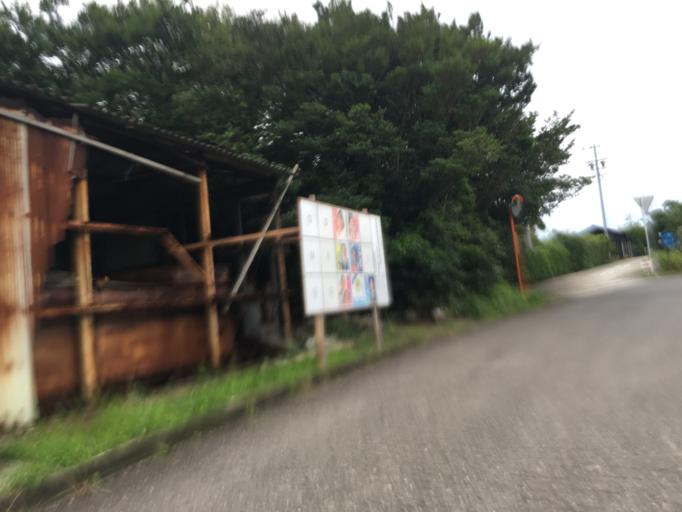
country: JP
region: Aichi
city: Ishiki
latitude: 34.7260
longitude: 137.0380
